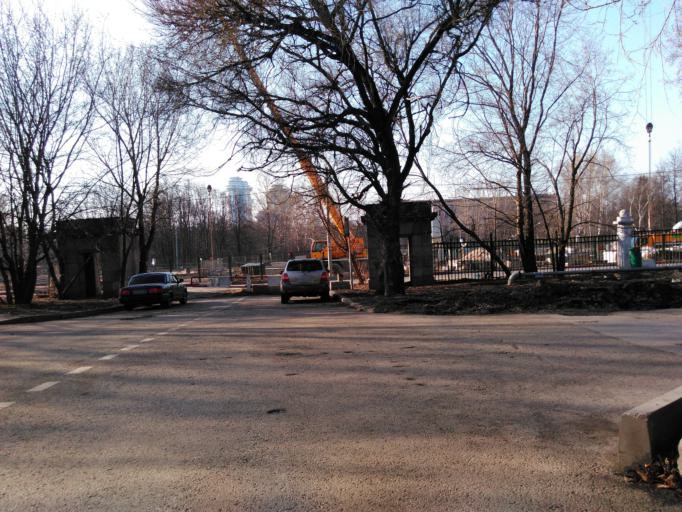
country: RU
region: Moscow
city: Vorob'yovo
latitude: 55.7077
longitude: 37.5195
